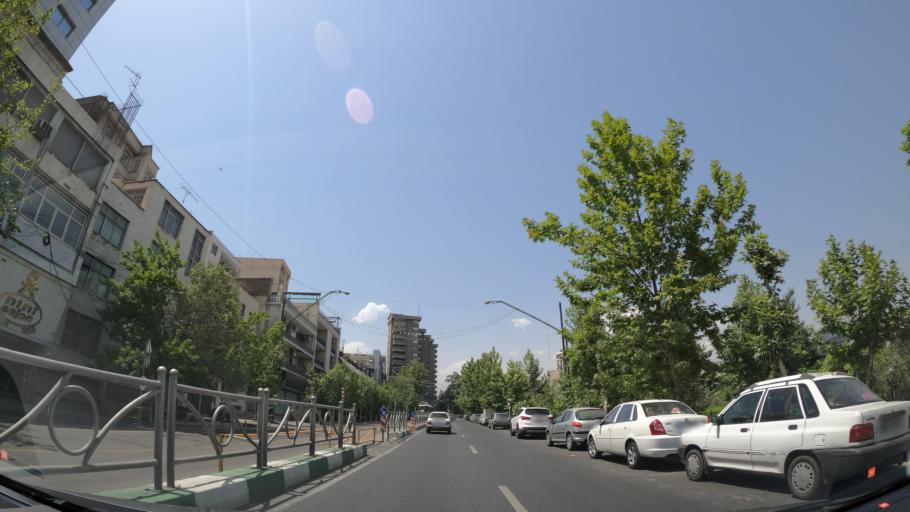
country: IR
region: Tehran
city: Tehran
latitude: 35.7355
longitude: 51.4098
